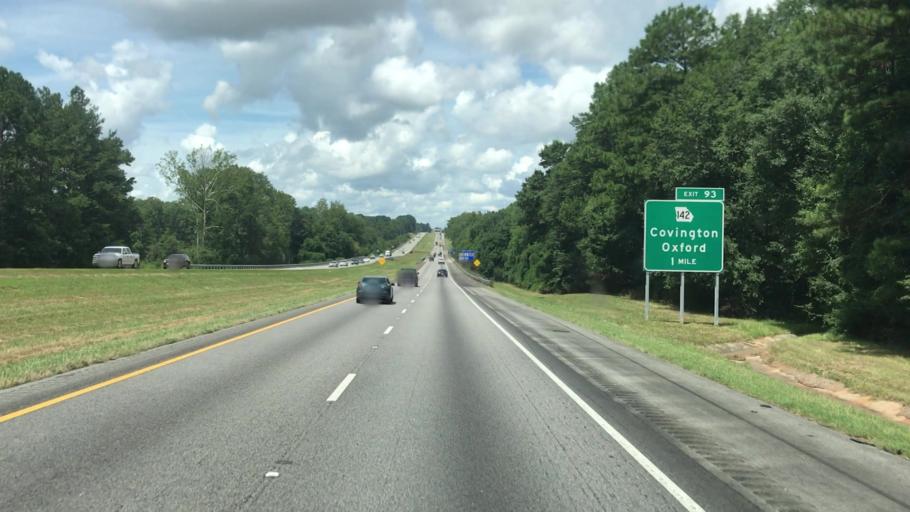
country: US
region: Georgia
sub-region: Newton County
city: Covington
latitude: 33.6106
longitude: -83.7997
